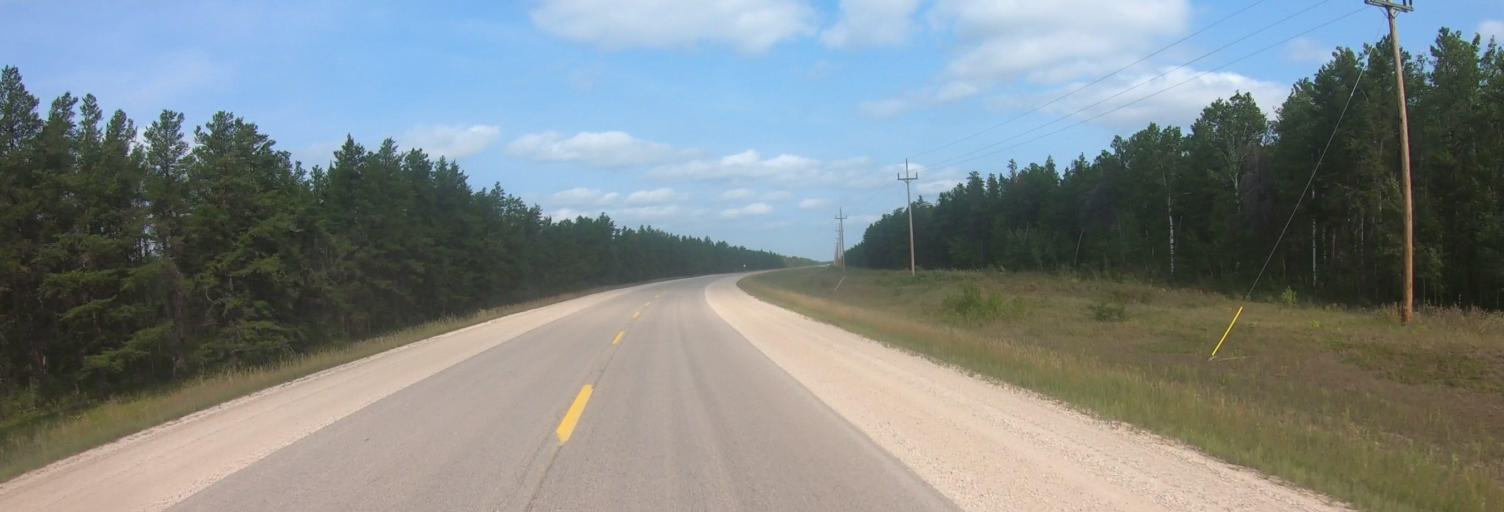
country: CA
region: Manitoba
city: La Broquerie
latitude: 49.2389
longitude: -96.3473
